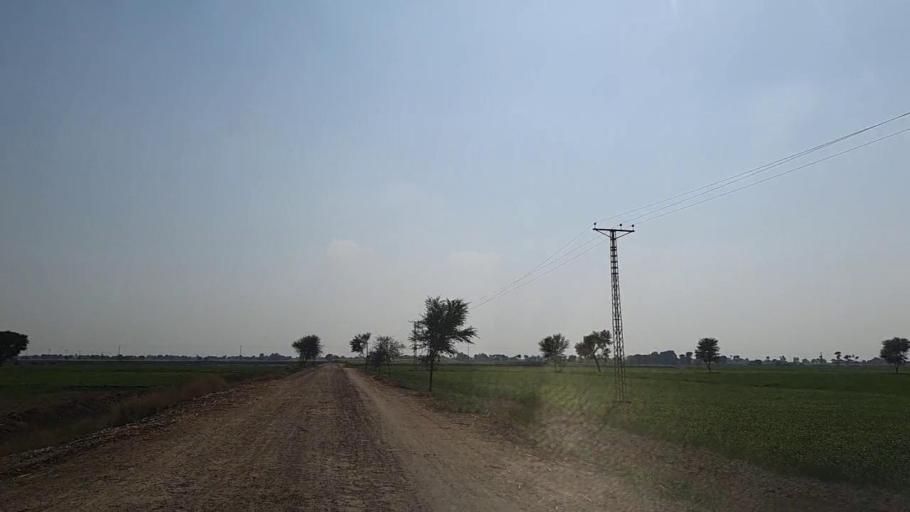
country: PK
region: Sindh
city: Daur
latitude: 26.4465
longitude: 68.2346
